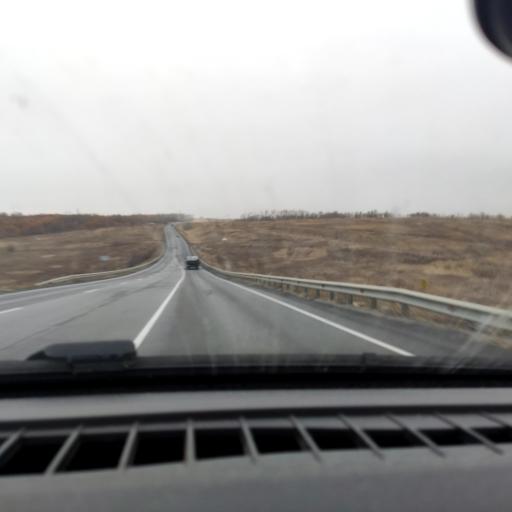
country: RU
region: Voronezj
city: Ostrogozhsk
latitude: 50.9353
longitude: 39.0566
